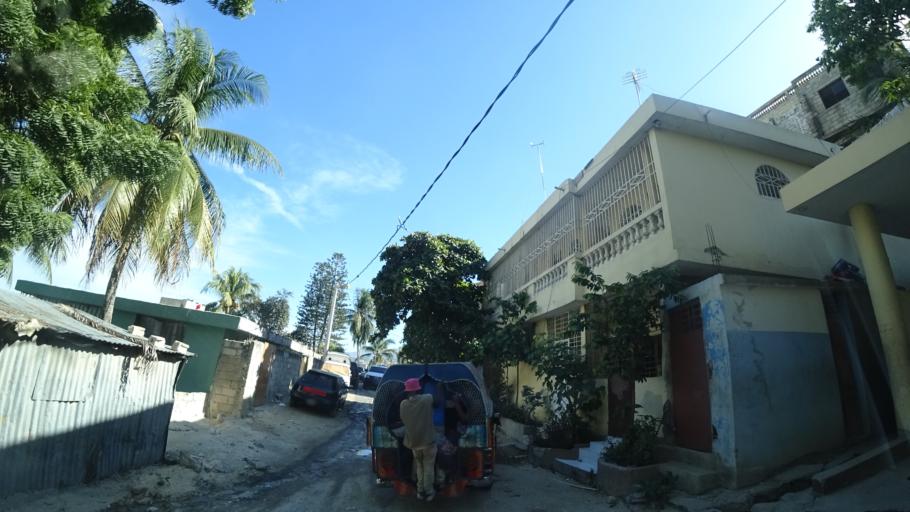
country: HT
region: Ouest
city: Delmas 73
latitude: 18.5513
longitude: -72.3166
